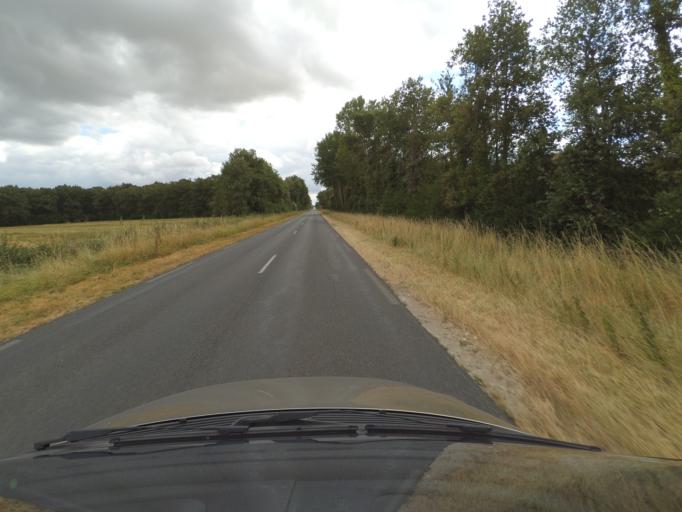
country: FR
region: Centre
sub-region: Departement d'Indre-et-Loire
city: Richelieu
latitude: 46.9798
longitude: 0.3524
